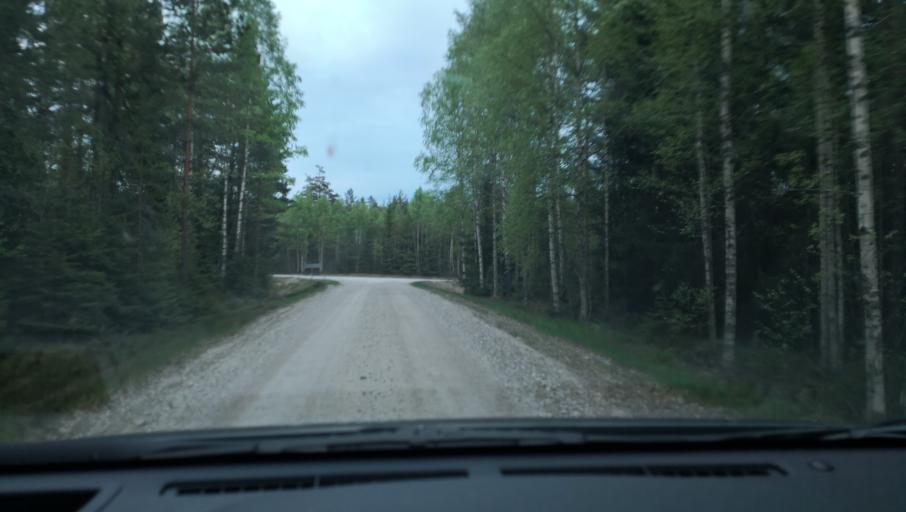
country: SE
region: Vaestmanland
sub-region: Skinnskattebergs Kommun
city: Skinnskatteberg
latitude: 59.7590
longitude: 15.4611
